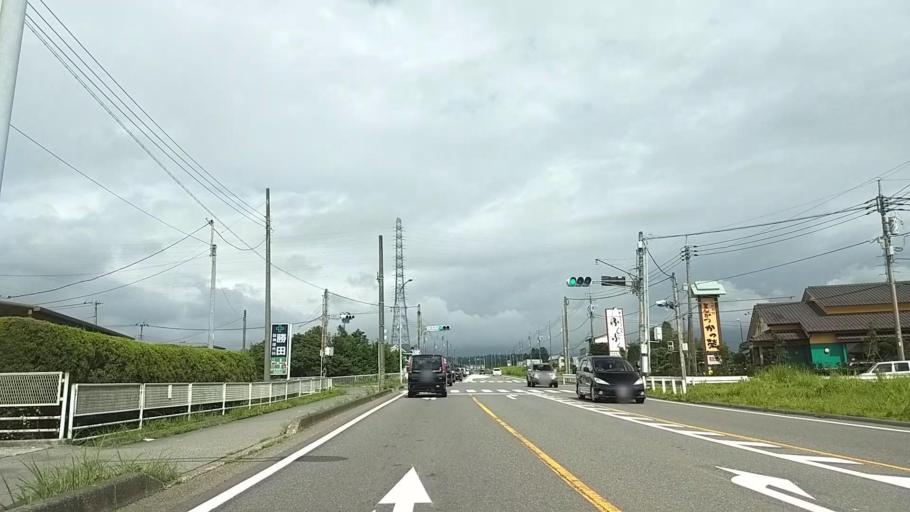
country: JP
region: Shizuoka
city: Gotemba
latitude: 35.3147
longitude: 138.9228
